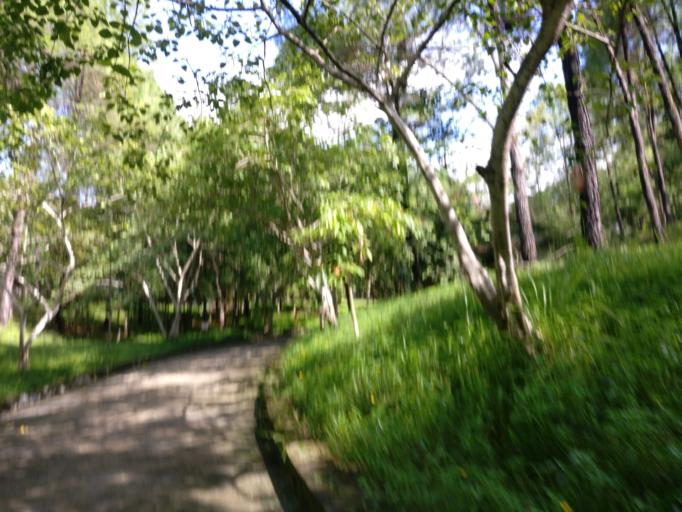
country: VN
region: Thua Thien-Hue
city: Hue
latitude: 16.4200
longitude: 107.6074
